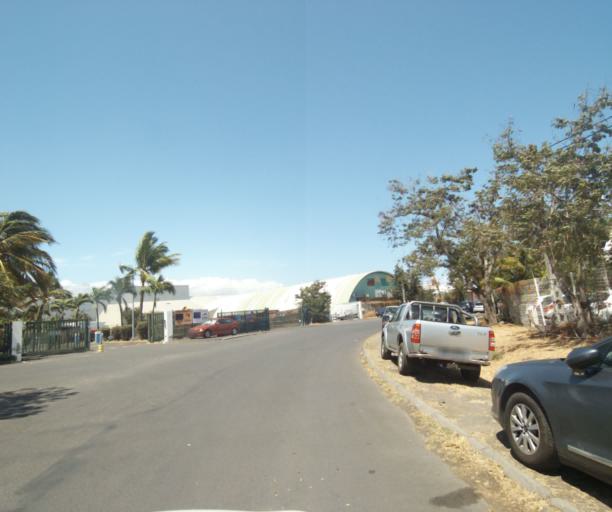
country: RE
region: Reunion
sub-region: Reunion
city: Le Port
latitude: -20.9630
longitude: 55.2991
